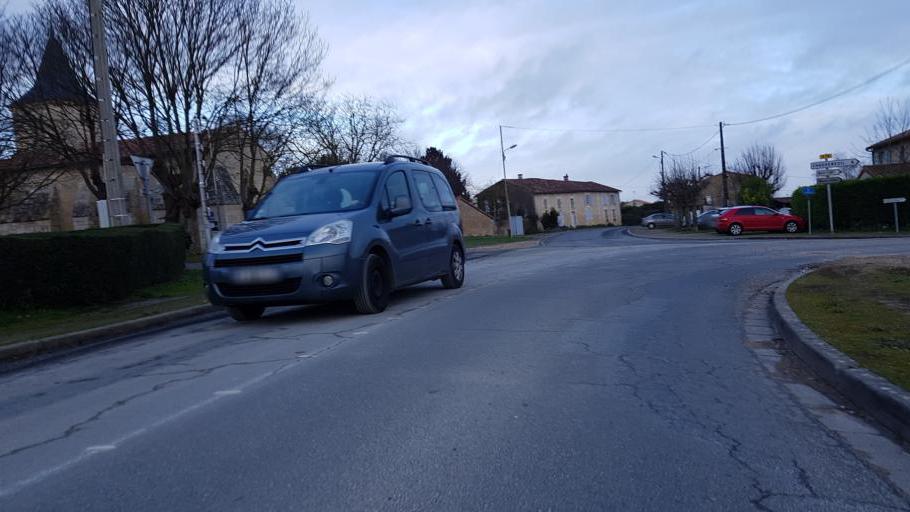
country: FR
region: Poitou-Charentes
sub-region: Departement de la Vienne
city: Avanton
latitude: 46.6642
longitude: 0.3087
